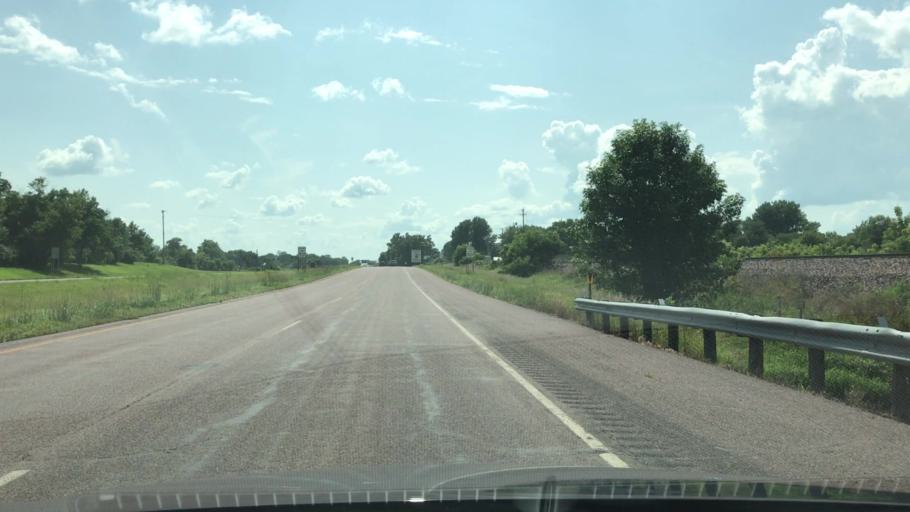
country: US
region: Minnesota
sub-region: Blue Earth County
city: Lake Crystal
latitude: 44.1184
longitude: -94.2052
